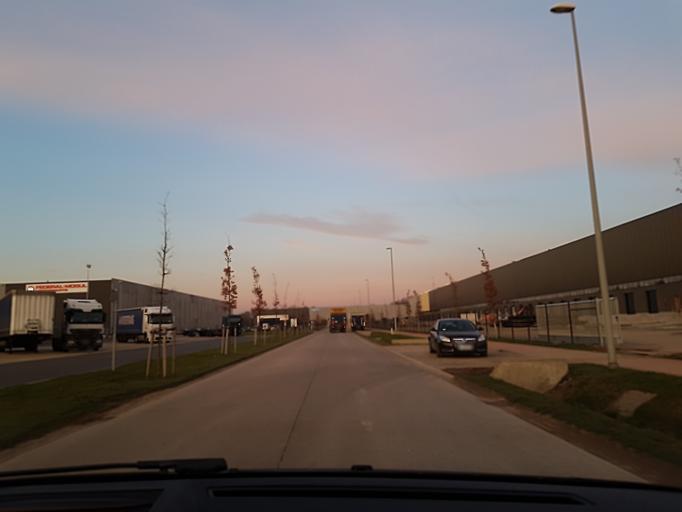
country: BE
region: Flanders
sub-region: Provincie Antwerpen
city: Willebroek
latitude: 51.0436
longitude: 4.3696
